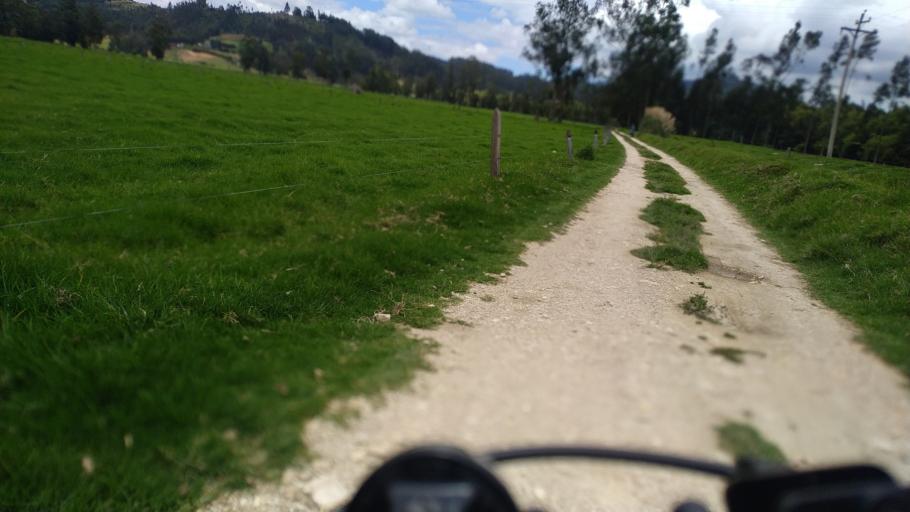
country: CO
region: Boyaca
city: Paipa
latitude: 5.7779
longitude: -73.0867
